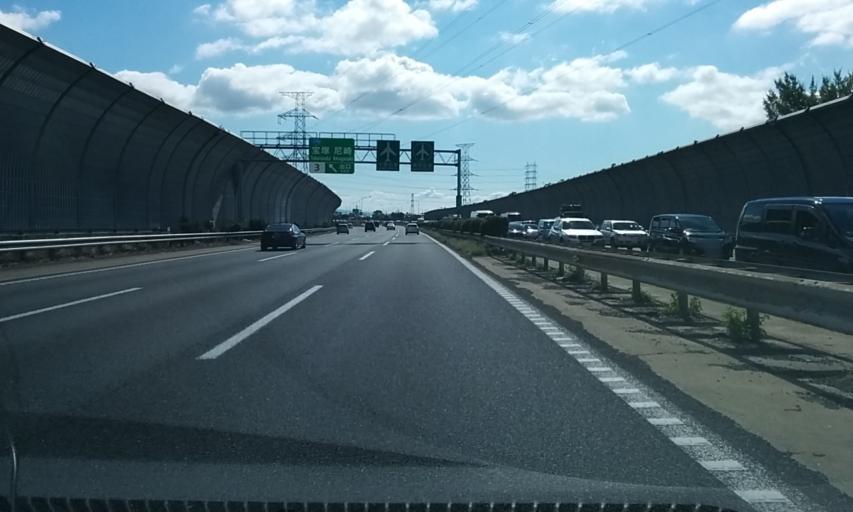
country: JP
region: Hyogo
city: Takarazuka
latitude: 34.8096
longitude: 135.3644
